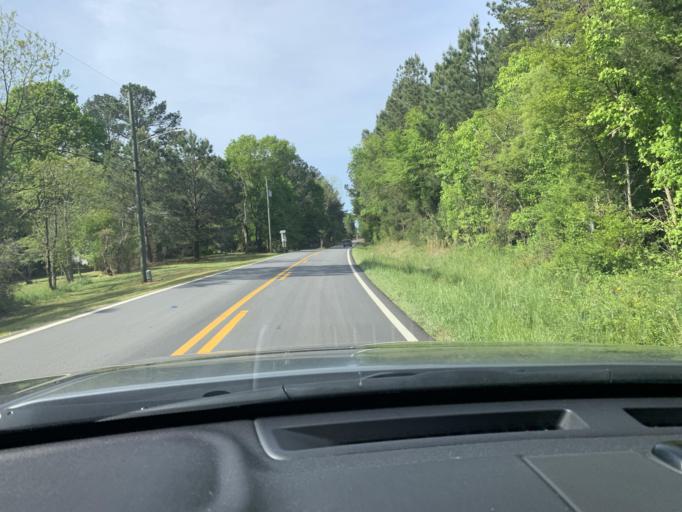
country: US
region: Georgia
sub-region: Oconee County
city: Watkinsville
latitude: 33.8154
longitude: -83.4426
